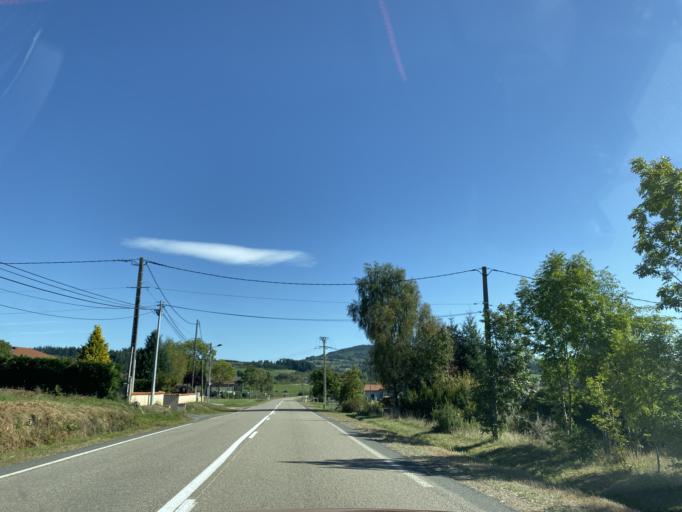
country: FR
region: Rhone-Alpes
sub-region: Departement de la Loire
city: Noiretable
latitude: 45.8496
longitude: 3.7997
